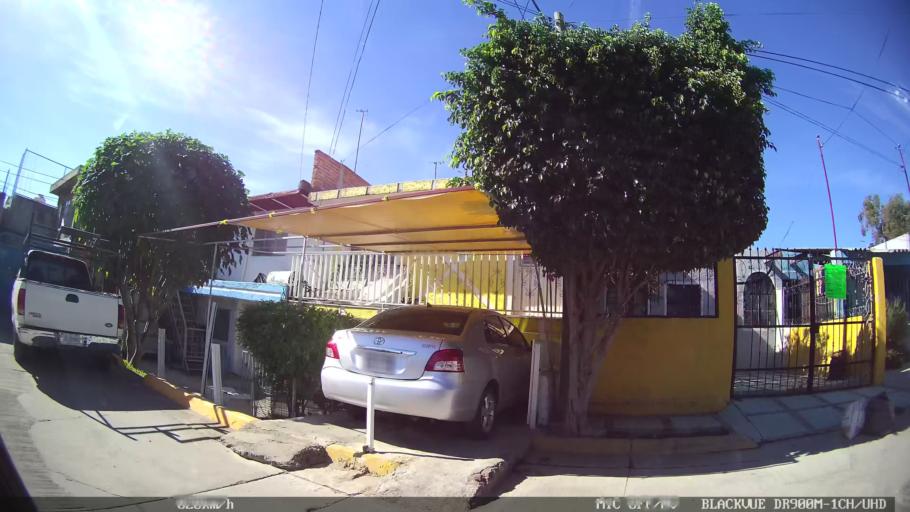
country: MX
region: Jalisco
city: Tlaquepaque
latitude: 20.6885
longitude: -103.2763
